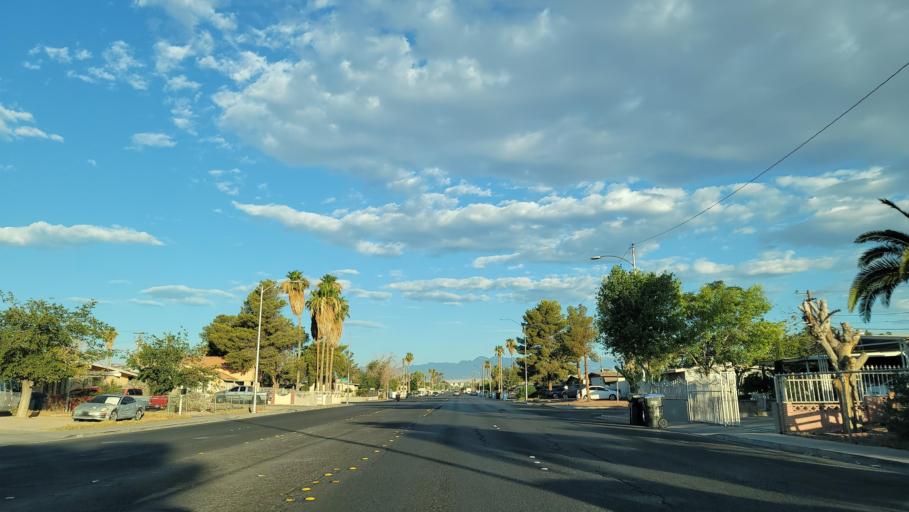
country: US
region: Nevada
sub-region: Clark County
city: North Las Vegas
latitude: 36.1883
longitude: -115.1025
